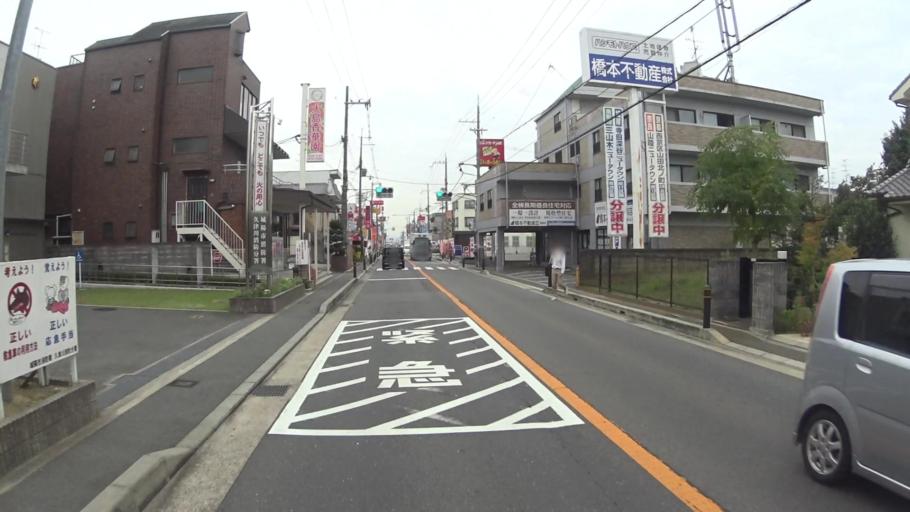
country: JP
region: Kyoto
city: Uji
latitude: 34.8633
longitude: 135.7769
